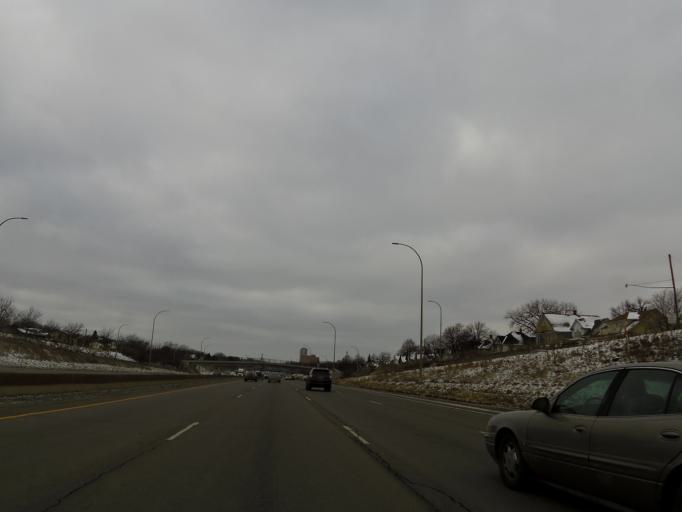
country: US
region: Minnesota
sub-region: Ramsey County
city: Saint Paul
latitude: 44.9514
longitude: -93.1277
